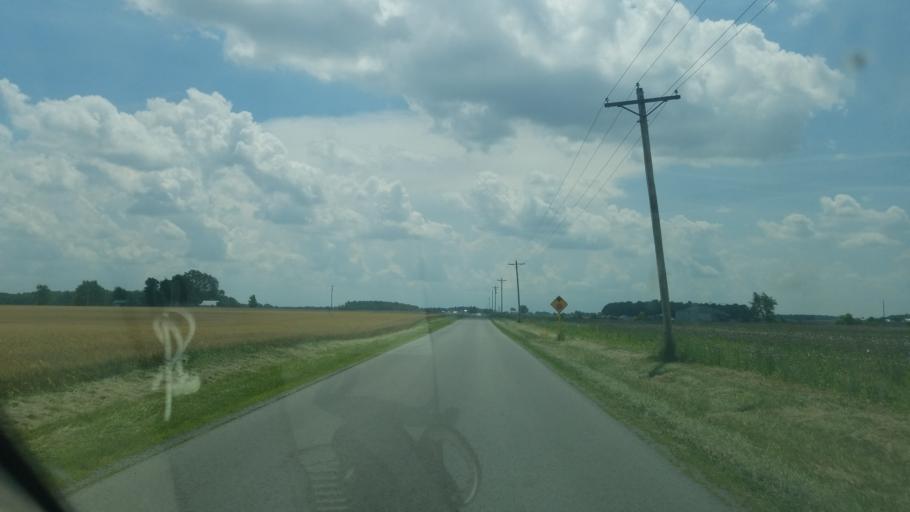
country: US
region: Ohio
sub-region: Hancock County
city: Arlington
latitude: 40.8361
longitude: -83.6000
